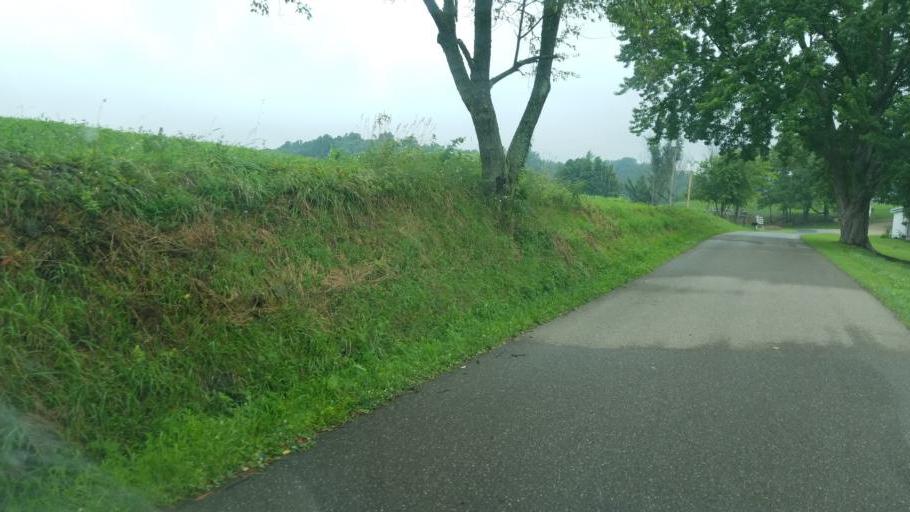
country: US
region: Ohio
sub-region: Columbiana County
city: Salineville
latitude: 40.5636
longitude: -80.8507
